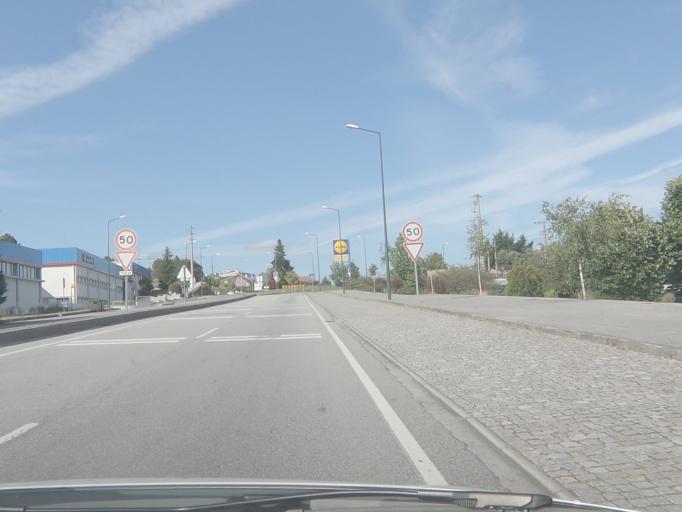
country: PT
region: Viseu
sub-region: Viseu
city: Viseu
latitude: 40.6330
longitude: -7.9316
